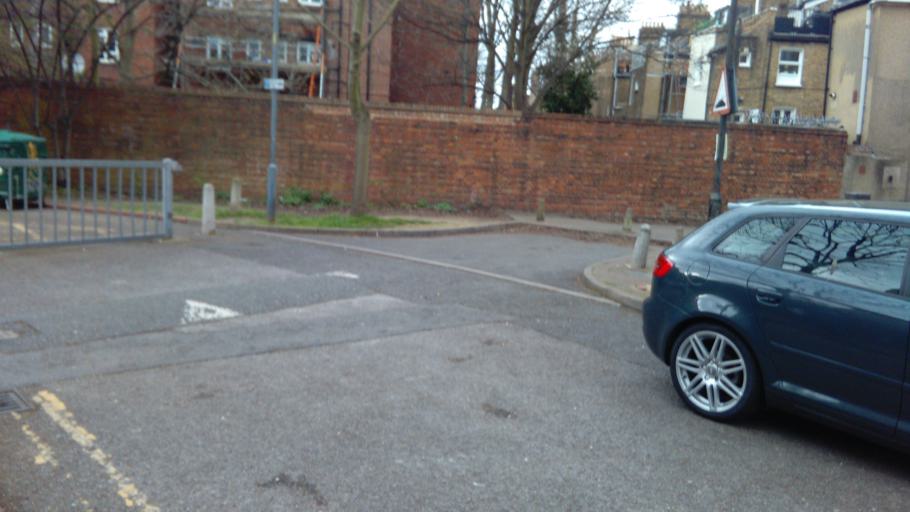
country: GB
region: England
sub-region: Greater London
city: Brixton Hill
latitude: 51.4612
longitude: -0.1315
